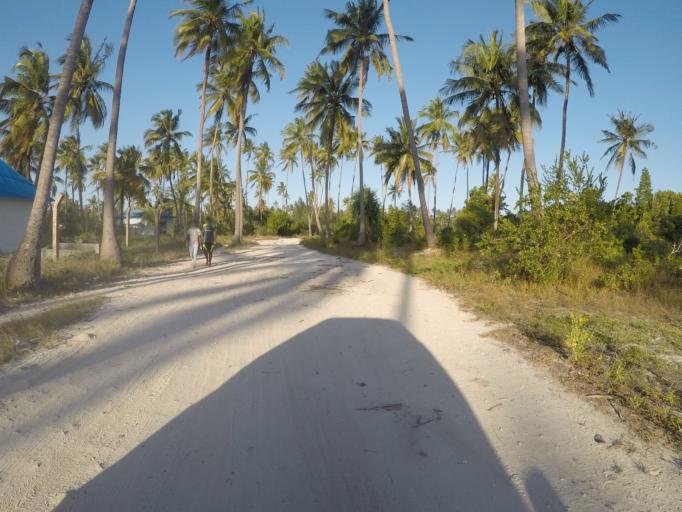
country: TZ
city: Kiwengwa
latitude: -6.1436
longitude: 39.4919
